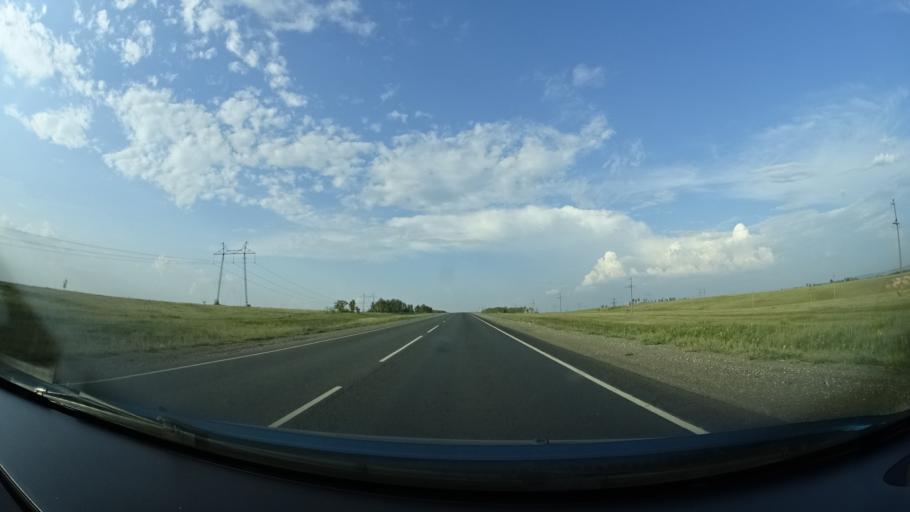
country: RU
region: Samara
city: Sukhodol
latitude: 53.7071
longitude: 50.8120
